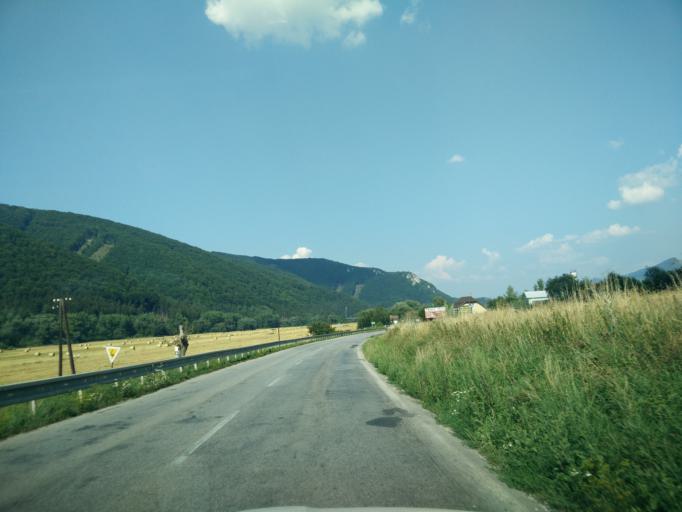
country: SK
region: Zilinsky
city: Rajec
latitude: 49.1214
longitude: 18.6634
